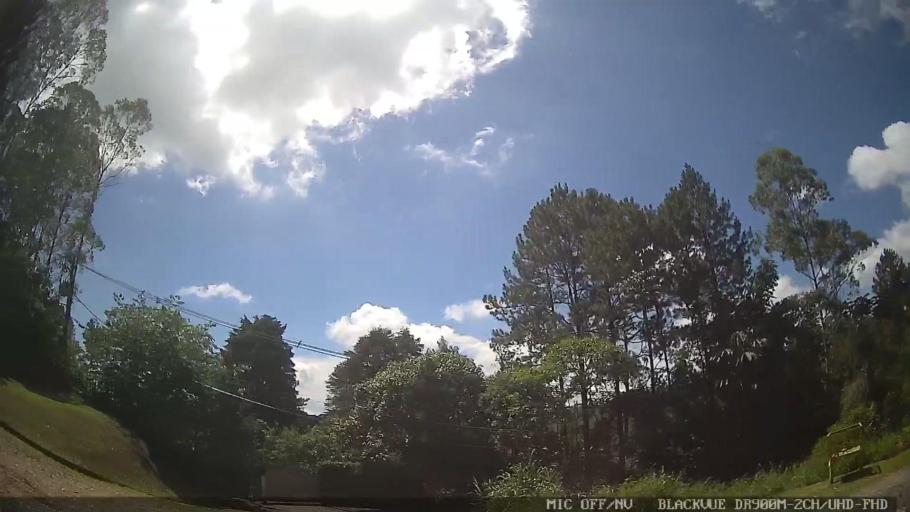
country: BR
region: Sao Paulo
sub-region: Mogi das Cruzes
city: Mogi das Cruzes
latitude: -23.6675
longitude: -46.2097
